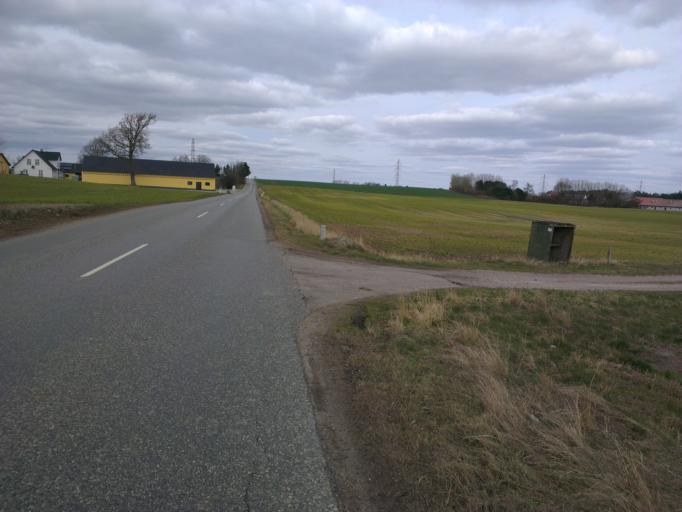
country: DK
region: Capital Region
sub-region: Frederikssund Kommune
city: Skibby
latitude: 55.7928
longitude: 12.0125
